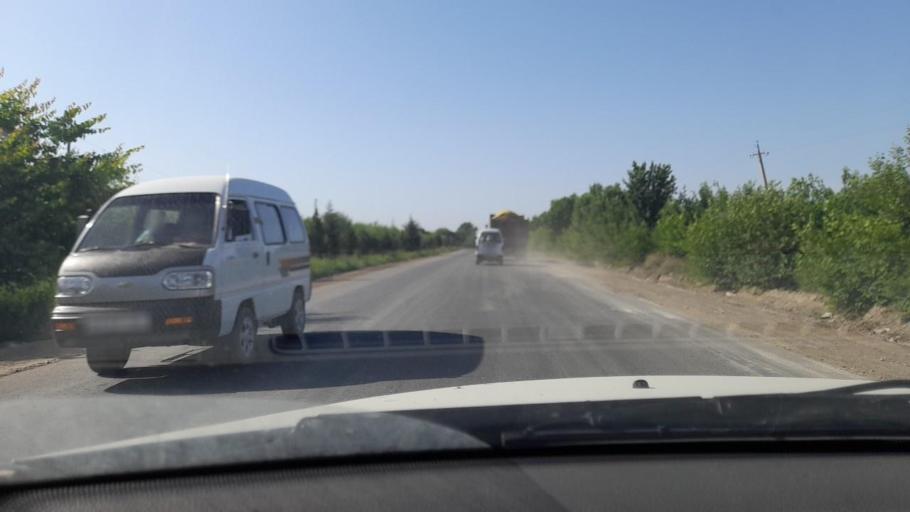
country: UZ
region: Bukhara
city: Romiton
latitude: 40.0525
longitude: 64.3282
